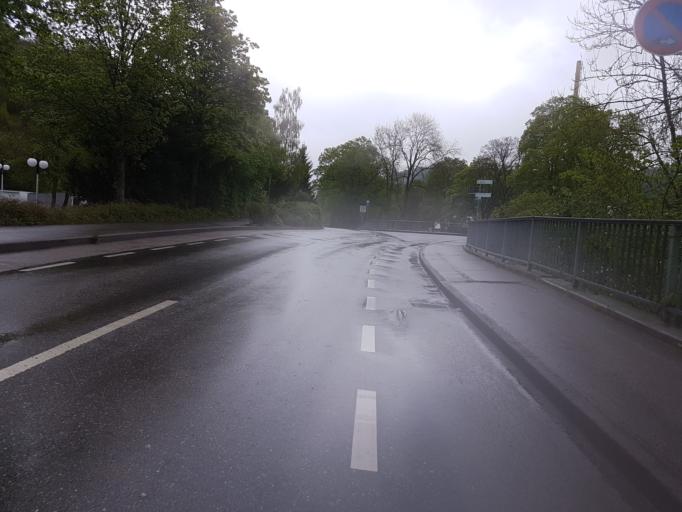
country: DE
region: Baden-Wuerttemberg
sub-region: Freiburg Region
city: Oberndorf
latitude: 48.2881
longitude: 8.5801
